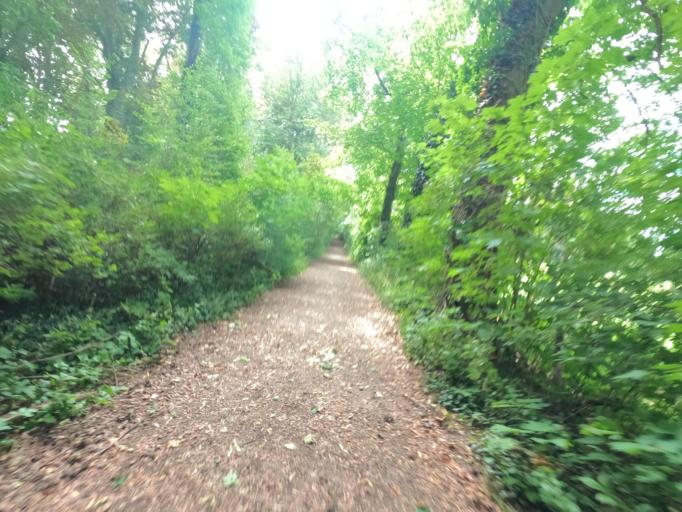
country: DE
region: North Rhine-Westphalia
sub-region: Regierungsbezirk Koln
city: Heinsberg
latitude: 51.0487
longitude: 6.1394
